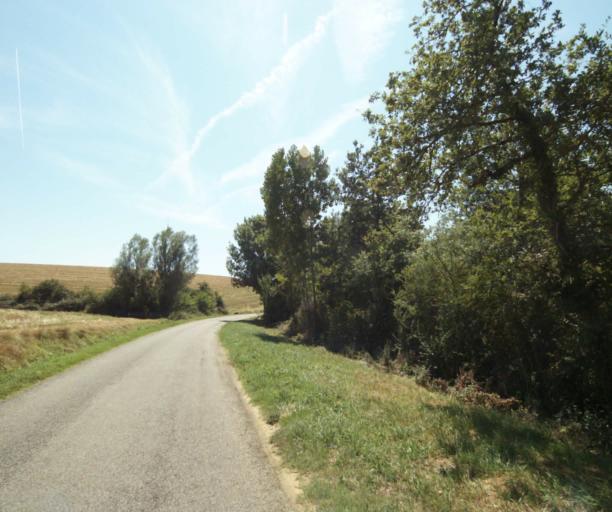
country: FR
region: Midi-Pyrenees
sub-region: Departement de l'Ariege
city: Lezat-sur-Leze
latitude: 43.2679
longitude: 1.3353
